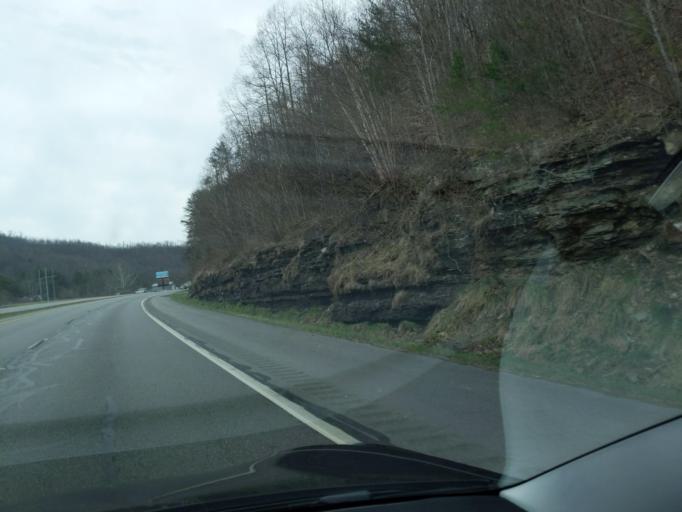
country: US
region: Kentucky
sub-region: Knox County
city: Barbourville
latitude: 36.8763
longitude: -83.8235
